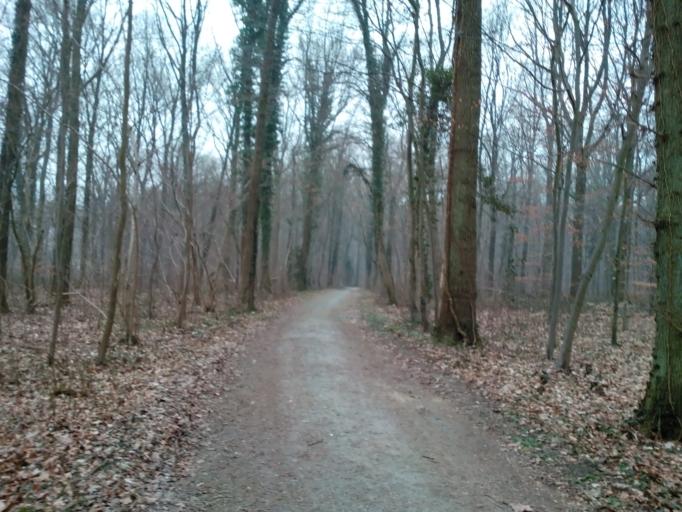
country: BE
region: Flanders
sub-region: Provincie Vlaams-Brabant
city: Oud-Heverlee
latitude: 50.8188
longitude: 4.7047
